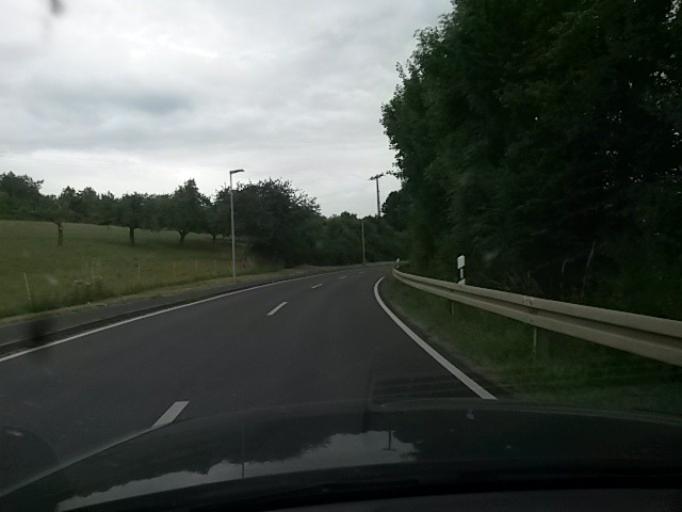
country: DE
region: Bavaria
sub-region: Regierungsbezirk Unterfranken
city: Rimpar
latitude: 49.8484
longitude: 9.9695
